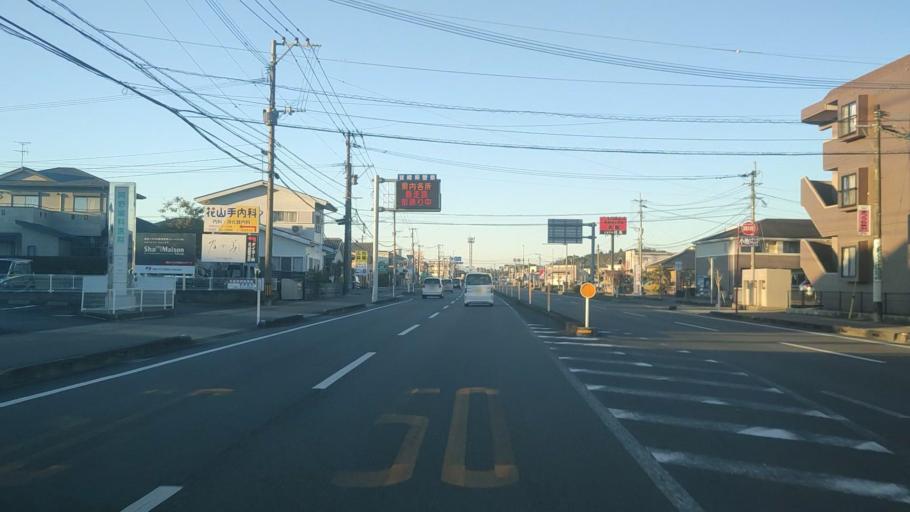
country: JP
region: Miyazaki
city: Miyazaki-shi
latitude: 31.8966
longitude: 131.4066
